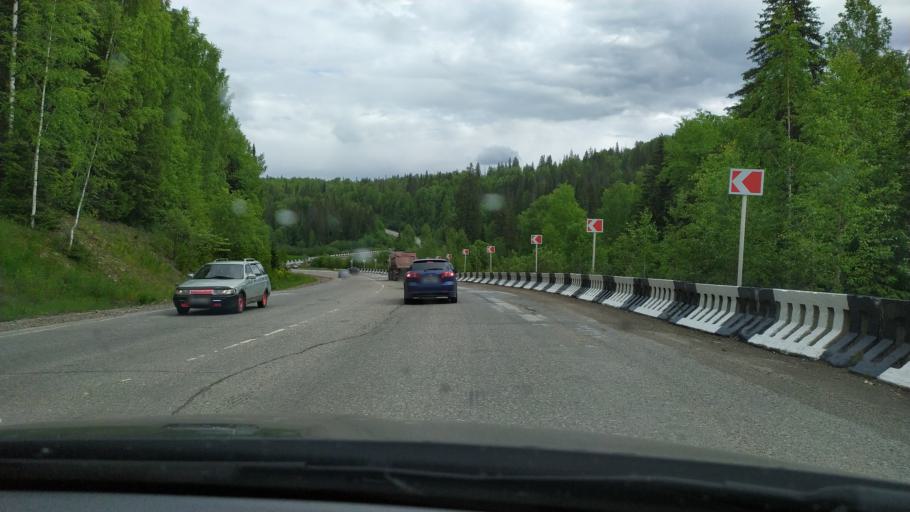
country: RU
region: Perm
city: Gremyachinsk
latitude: 58.4417
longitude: 57.8698
